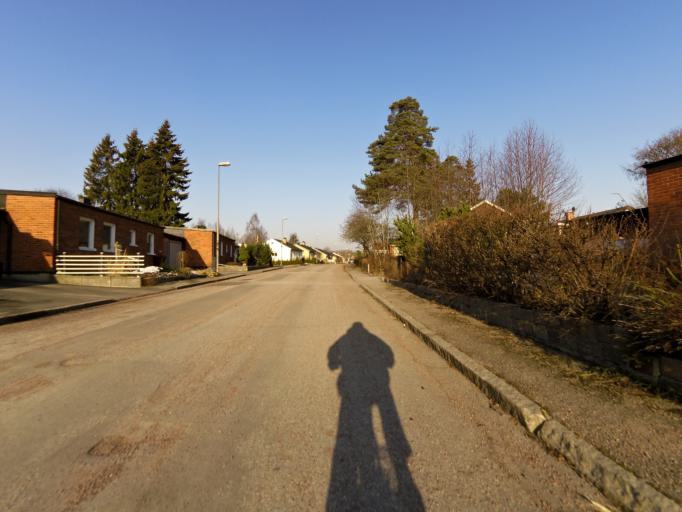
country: SE
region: Gaevleborg
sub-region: Gavle Kommun
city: Gavle
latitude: 60.6593
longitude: 17.1259
